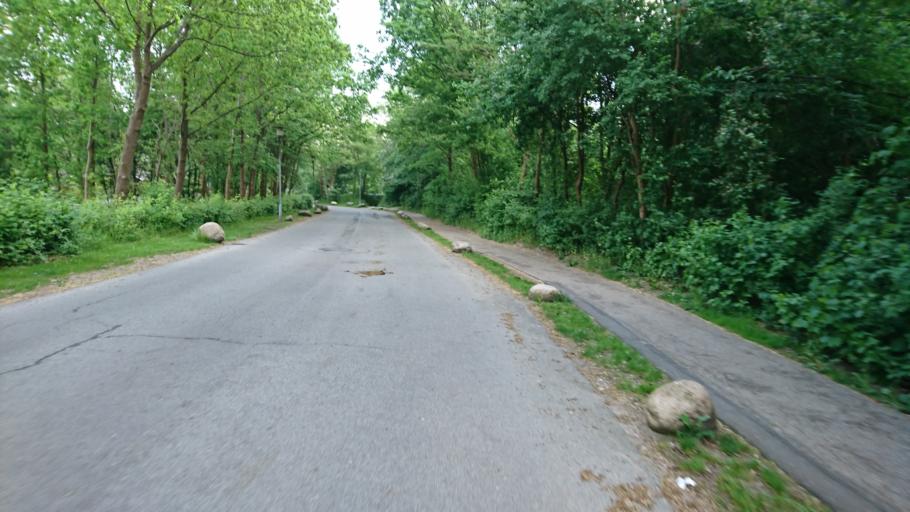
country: DK
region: Capital Region
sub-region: Ballerup Kommune
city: Ballerup
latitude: 55.7513
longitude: 12.4024
